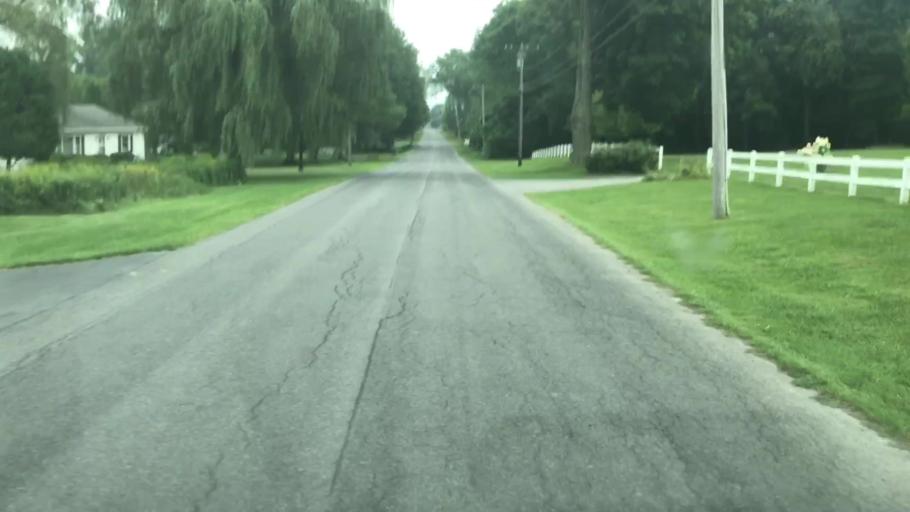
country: US
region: New York
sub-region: Onondaga County
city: Skaneateles
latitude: 42.9541
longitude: -76.4536
